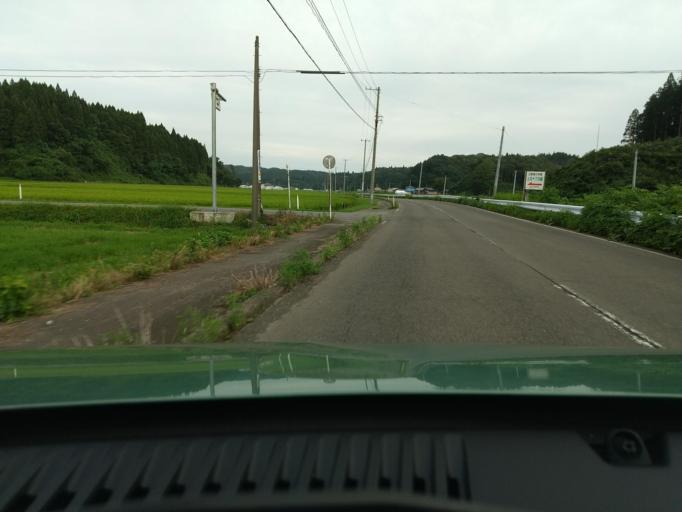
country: JP
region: Akita
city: Akita
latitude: 39.7877
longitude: 140.1210
